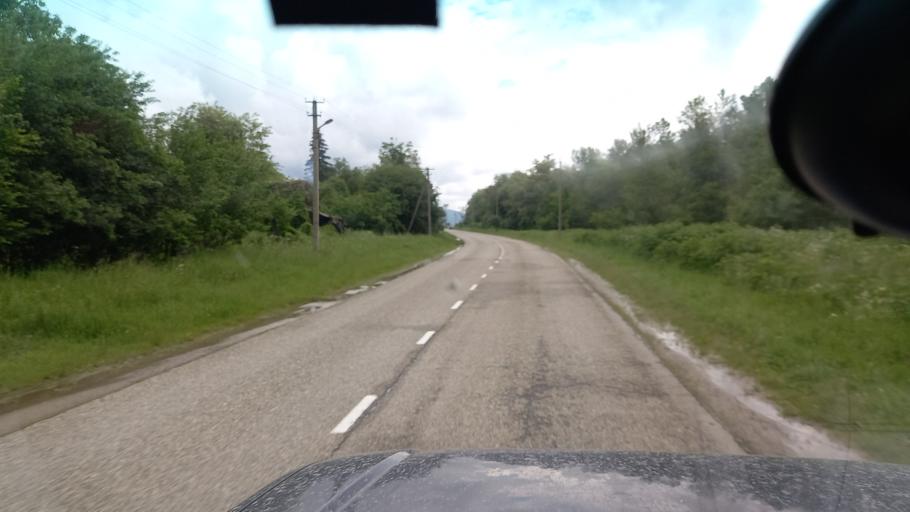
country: RU
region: Krasnodarskiy
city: Psebay
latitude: 44.0556
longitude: 40.7696
